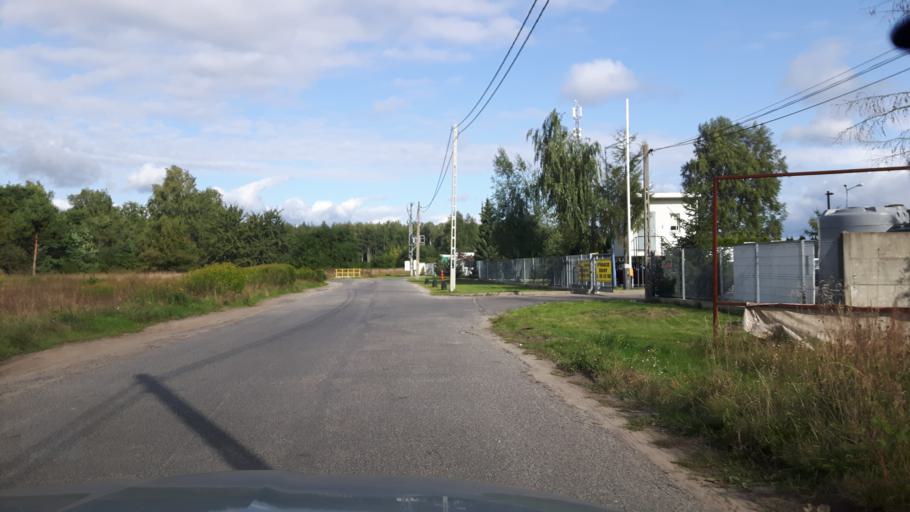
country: PL
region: Masovian Voivodeship
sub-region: Powiat wolominski
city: Marki
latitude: 52.3332
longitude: 21.0913
